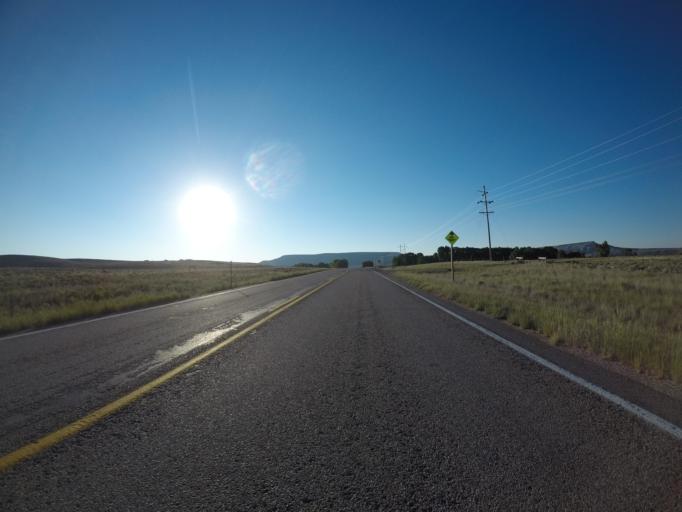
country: US
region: Wyoming
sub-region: Sublette County
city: Marbleton
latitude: 42.5703
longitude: -109.9614
